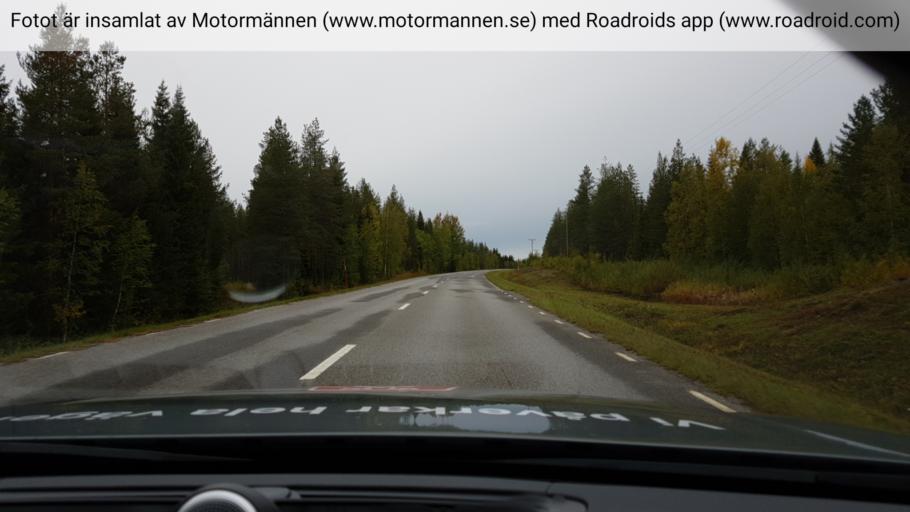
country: SE
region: Jaemtland
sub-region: Stroemsunds Kommun
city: Stroemsund
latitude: 64.2561
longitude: 15.4060
